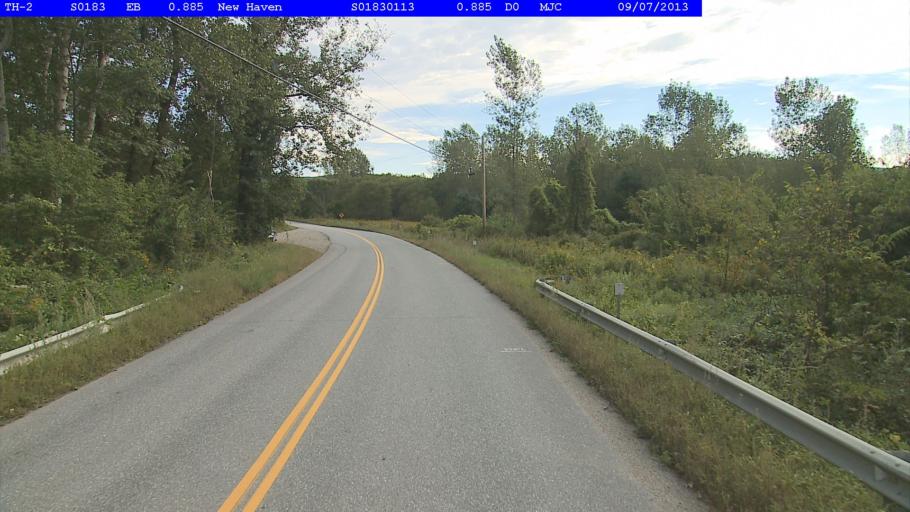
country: US
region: Vermont
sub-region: Addison County
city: Middlebury (village)
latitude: 44.0592
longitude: -73.1508
